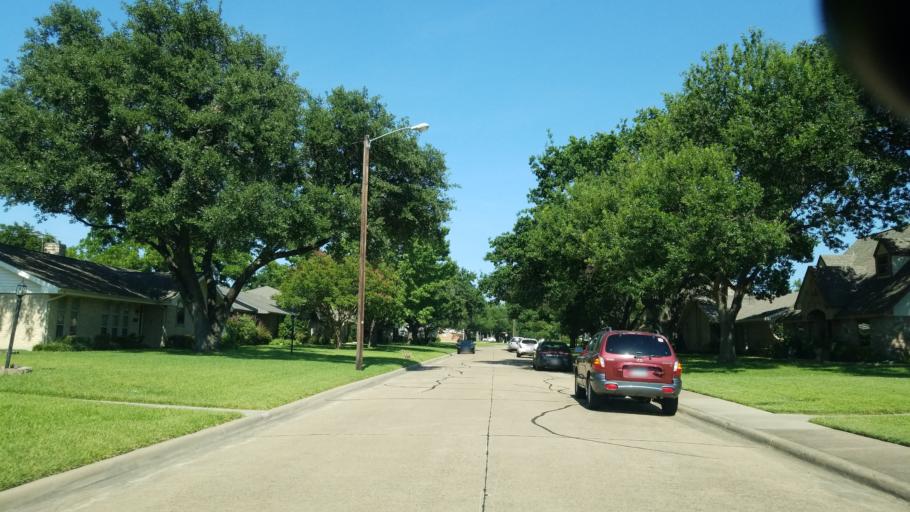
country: US
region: Texas
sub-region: Dallas County
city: Farmers Branch
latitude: 32.9195
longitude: -96.8836
